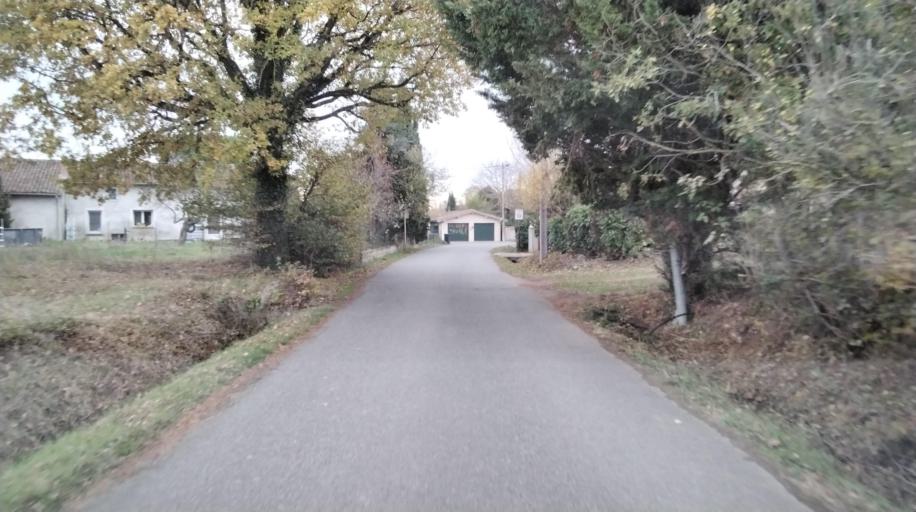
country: FR
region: Midi-Pyrenees
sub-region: Departement de la Haute-Garonne
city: Berat
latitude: 43.3873
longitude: 1.1886
